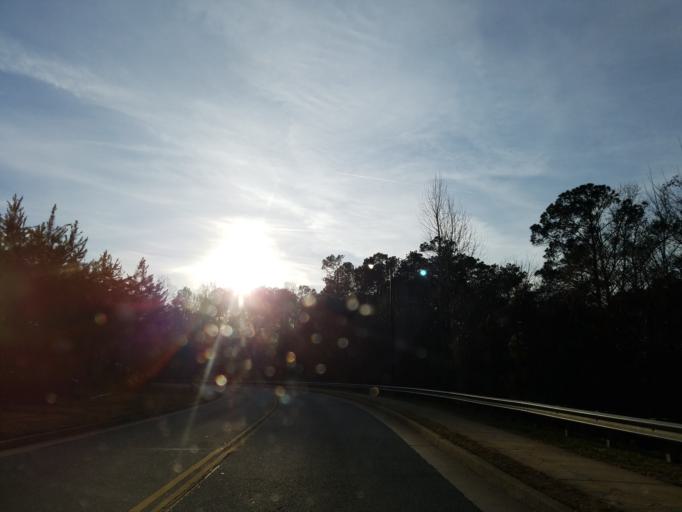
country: US
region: Georgia
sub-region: Cobb County
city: Acworth
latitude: 34.0678
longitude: -84.6661
